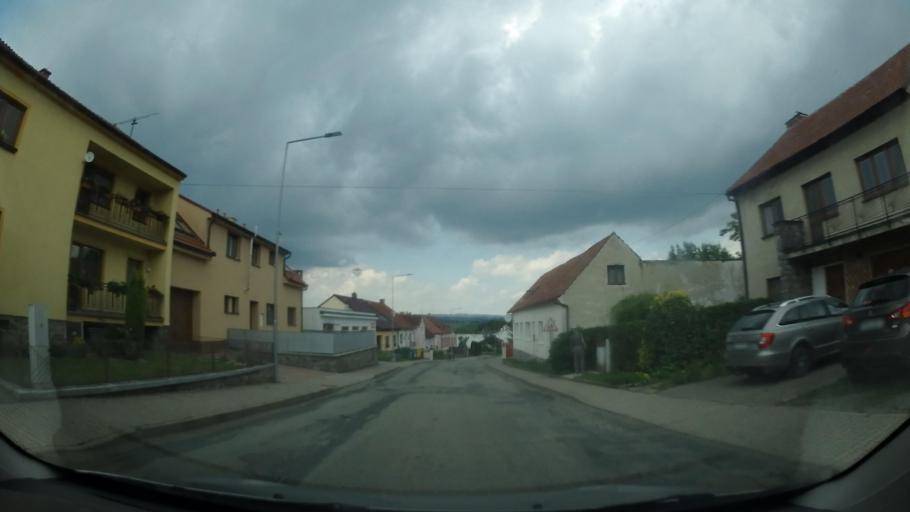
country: CZ
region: South Moravian
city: Svitavka
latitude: 49.4658
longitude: 16.6057
